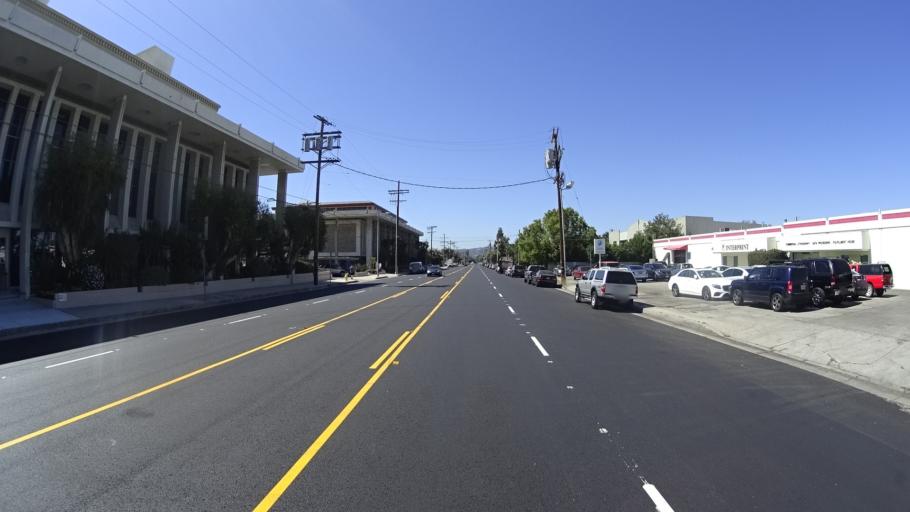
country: US
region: California
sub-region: Los Angeles County
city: Van Nuys
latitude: 34.2001
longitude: -118.4925
